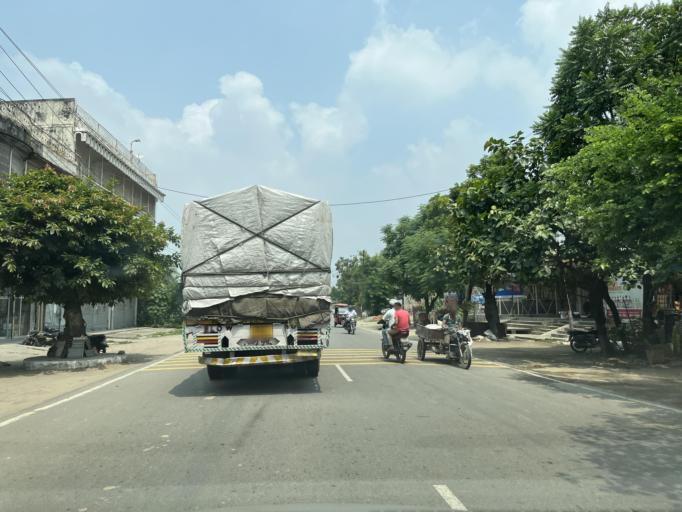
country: IN
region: Uttar Pradesh
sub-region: Bijnor
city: Najibabad
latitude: 29.5983
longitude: 78.3396
